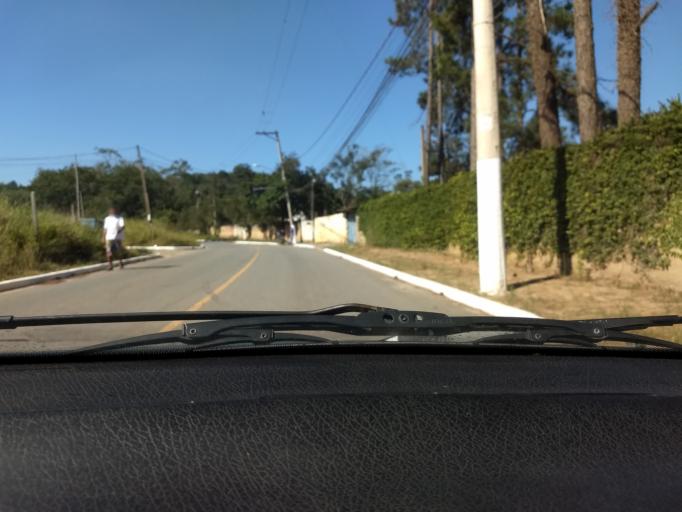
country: BR
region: Sao Paulo
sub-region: Embu-Guacu
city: Embu Guacu
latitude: -23.8110
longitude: -46.7567
